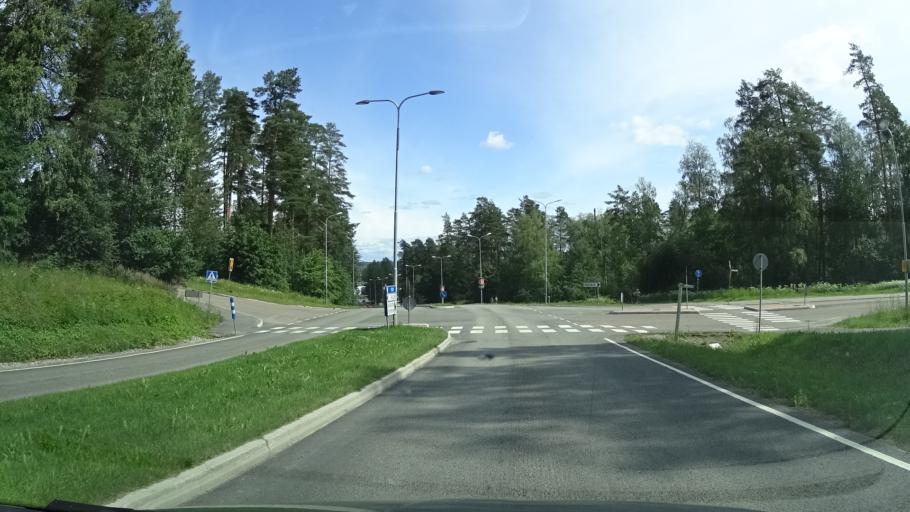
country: FI
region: Central Finland
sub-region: Jyvaeskylae
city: Jyvaeskylae
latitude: 62.2413
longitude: 25.6985
